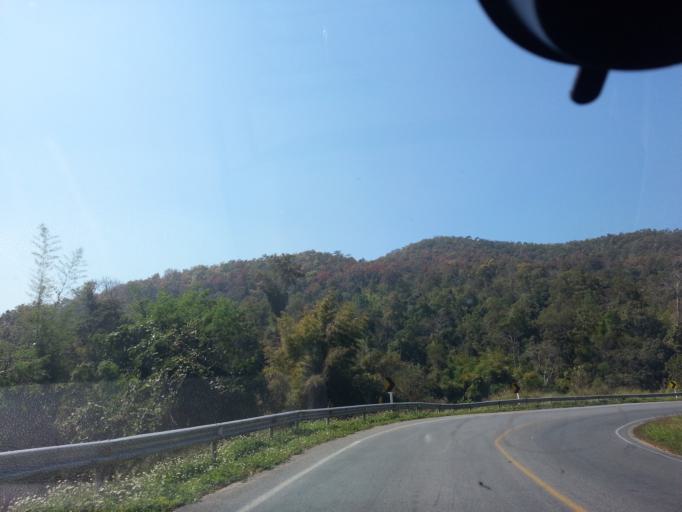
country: TH
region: Chiang Mai
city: Chai Prakan
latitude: 19.5691
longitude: 99.0794
